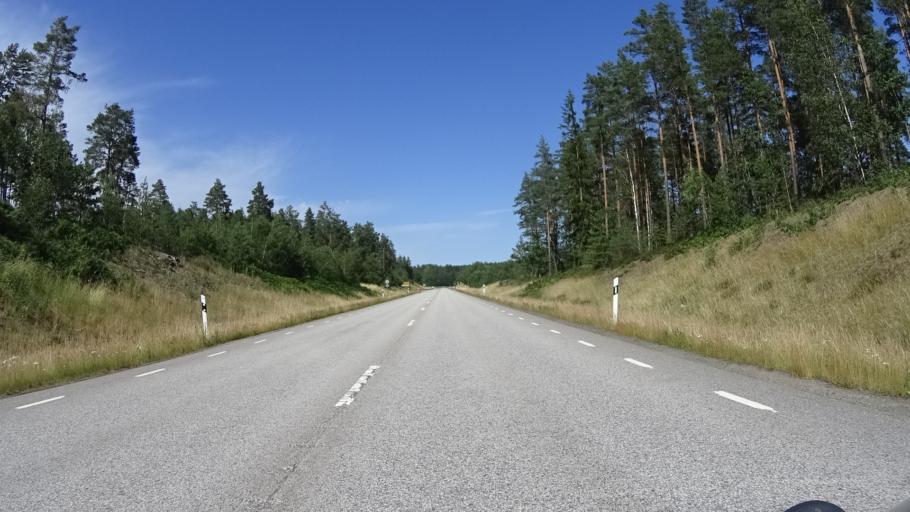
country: SE
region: Kalmar
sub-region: Vasterviks Kommun
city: Gamleby
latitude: 57.9329
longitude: 16.3800
